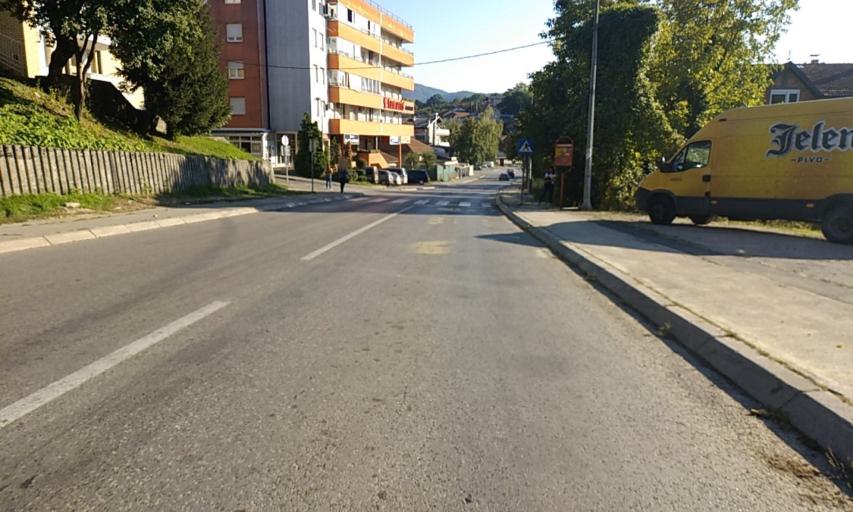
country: BA
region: Republika Srpska
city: Banja Luka
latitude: 44.7748
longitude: 17.1783
